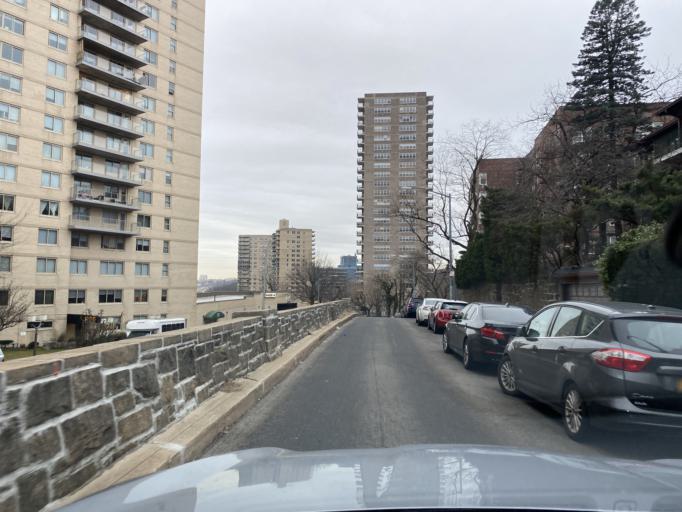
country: US
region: New York
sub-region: New York County
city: Inwood
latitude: 40.8791
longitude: -73.9151
